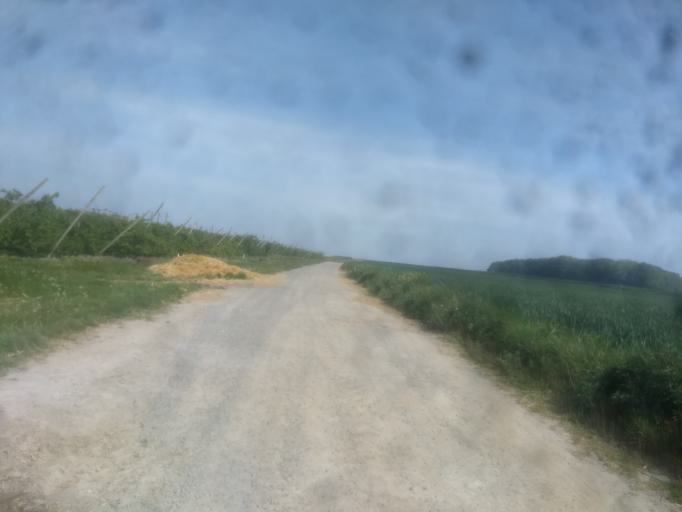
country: FR
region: Nord-Pas-de-Calais
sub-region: Departement du Pas-de-Calais
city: Beaurains
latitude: 50.2616
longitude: 2.8070
